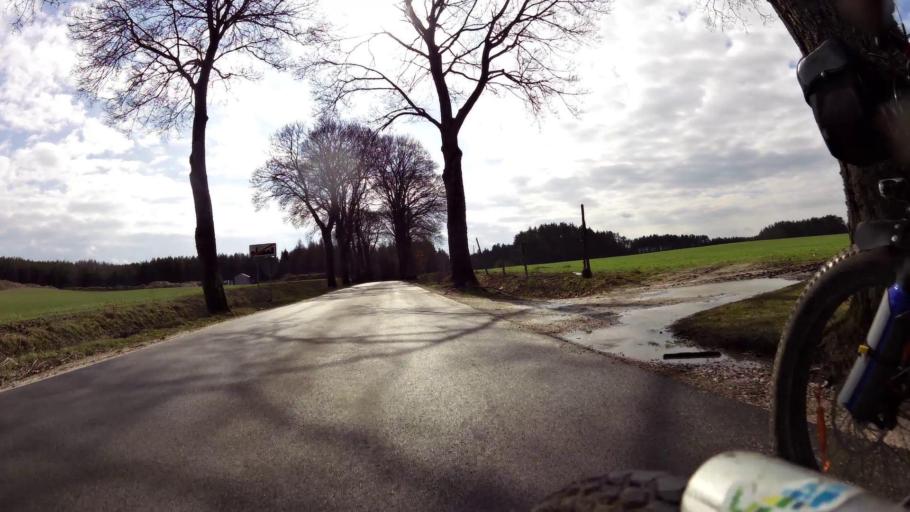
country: PL
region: Pomeranian Voivodeship
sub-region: Powiat bytowski
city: Kolczyglowy
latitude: 54.2090
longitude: 17.2353
